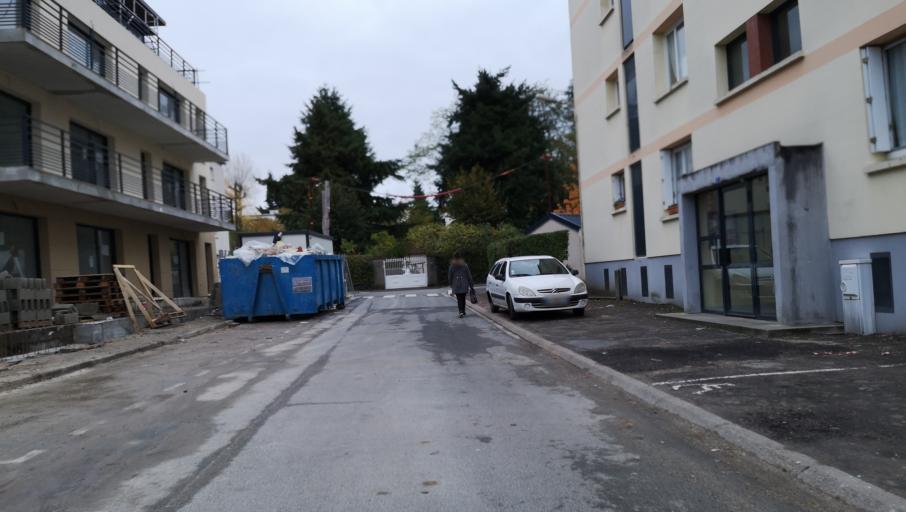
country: FR
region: Centre
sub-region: Departement du Loiret
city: Saint-Jean-de-Braye
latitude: 47.9101
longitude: 1.9705
